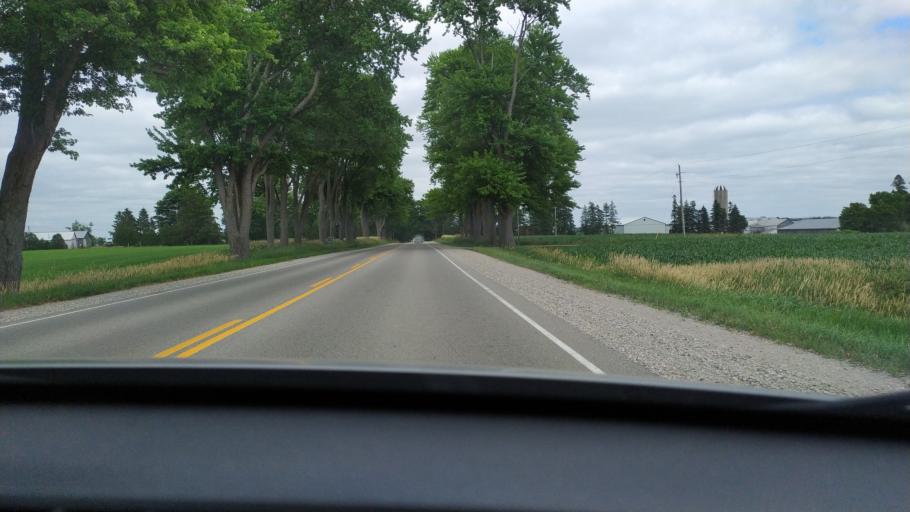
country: CA
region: Ontario
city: Stratford
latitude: 43.3159
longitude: -80.9668
